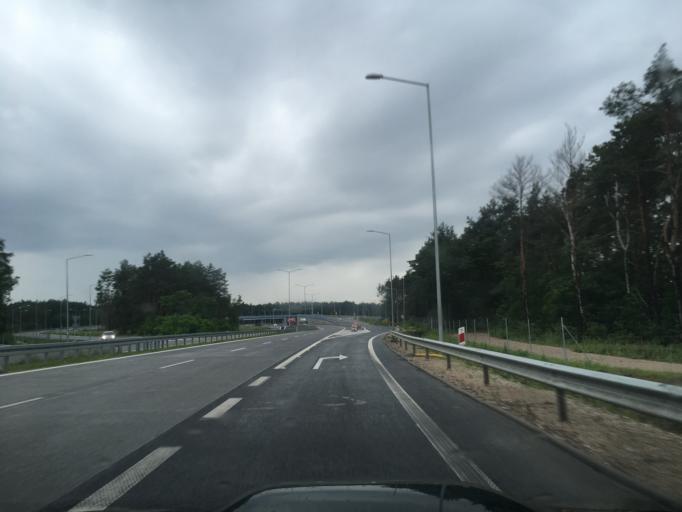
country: PL
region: Masovian Voivodeship
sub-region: Powiat piaseczynski
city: Gora Kalwaria
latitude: 51.9698
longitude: 21.2025
